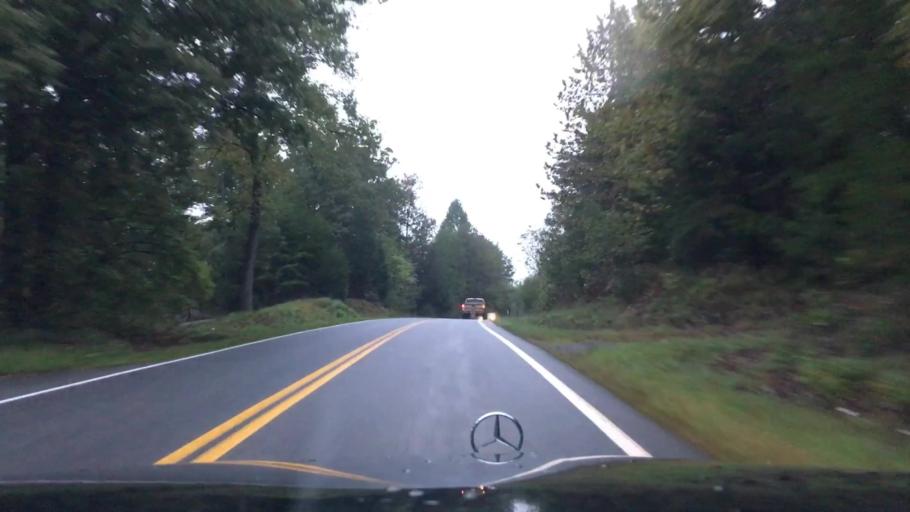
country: US
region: Virginia
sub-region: Campbell County
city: Timberlake
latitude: 37.2384
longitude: -79.2808
